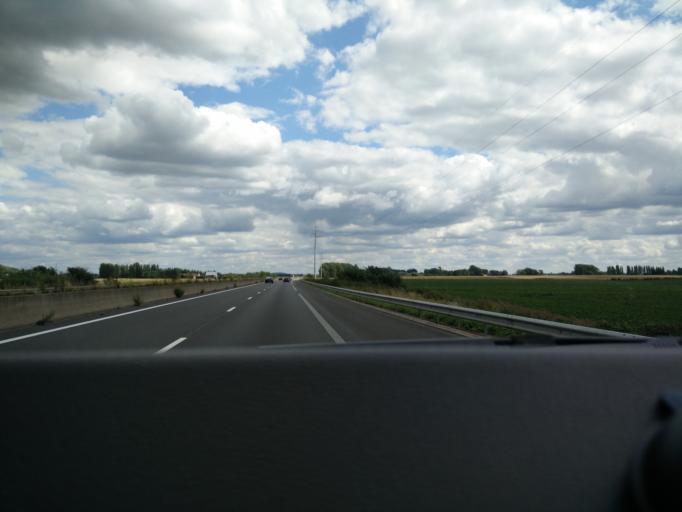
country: FR
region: Nord-Pas-de-Calais
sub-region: Departement du Nord
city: Wormhout
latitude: 50.8990
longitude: 2.4993
